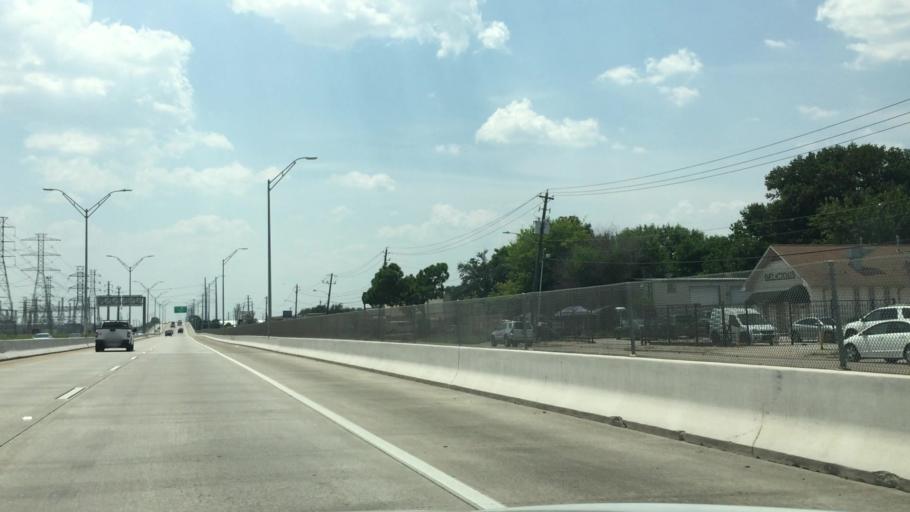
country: US
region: Texas
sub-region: Harris County
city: Piney Point Village
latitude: 29.7206
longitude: -95.5292
